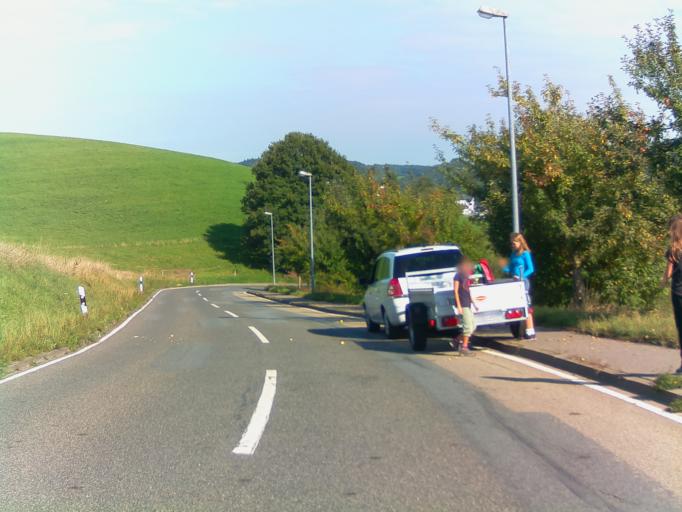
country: DE
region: Baden-Wuerttemberg
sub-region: Karlsruhe Region
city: Wilhelmsfeld
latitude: 49.5134
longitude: 8.7450
